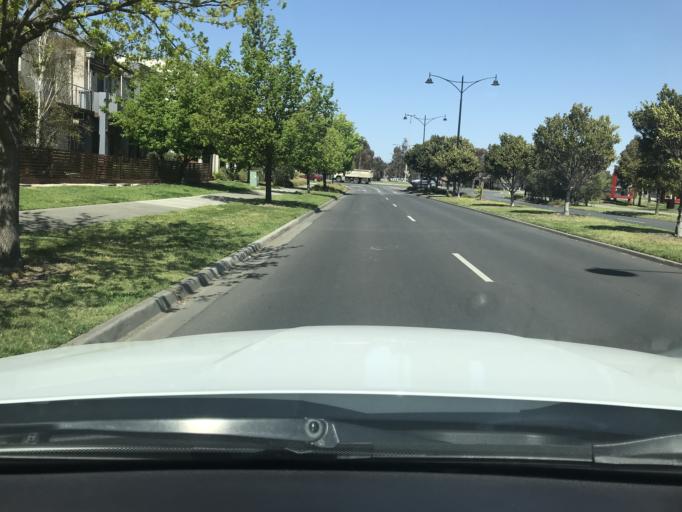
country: AU
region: Victoria
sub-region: Hume
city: Roxburgh Park
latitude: -37.5921
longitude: 144.9055
